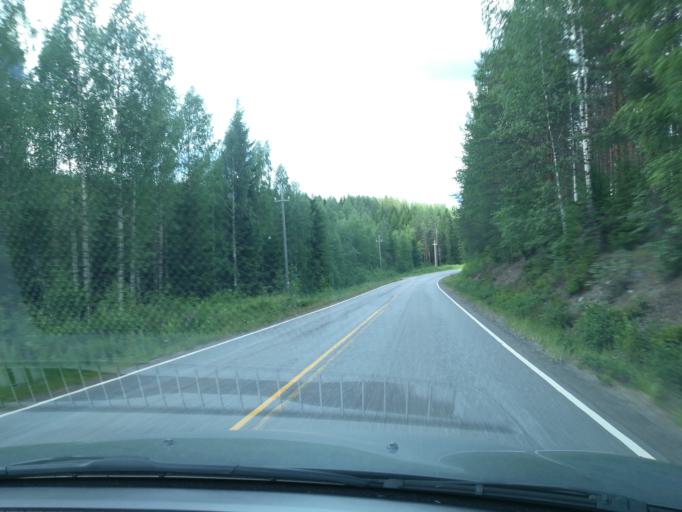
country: FI
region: Southern Savonia
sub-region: Mikkeli
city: Ristiina
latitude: 61.3459
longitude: 27.1659
